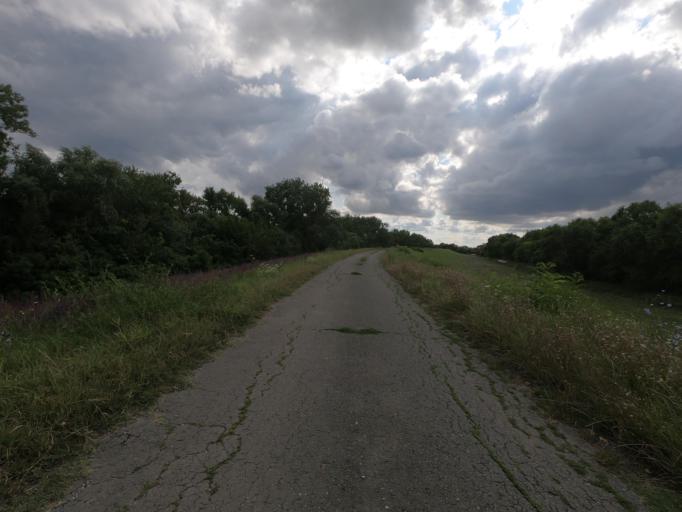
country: HU
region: Heves
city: Poroszlo
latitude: 47.6655
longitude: 20.6929
